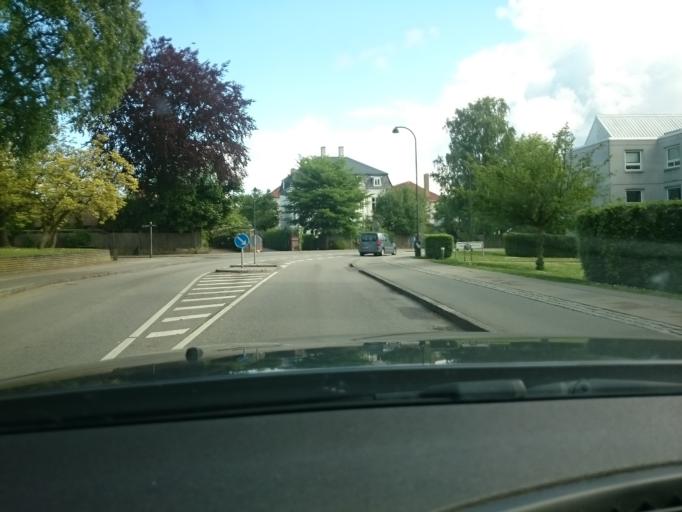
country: DK
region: Capital Region
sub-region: Gentofte Kommune
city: Charlottenlund
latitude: 55.7544
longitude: 12.5731
